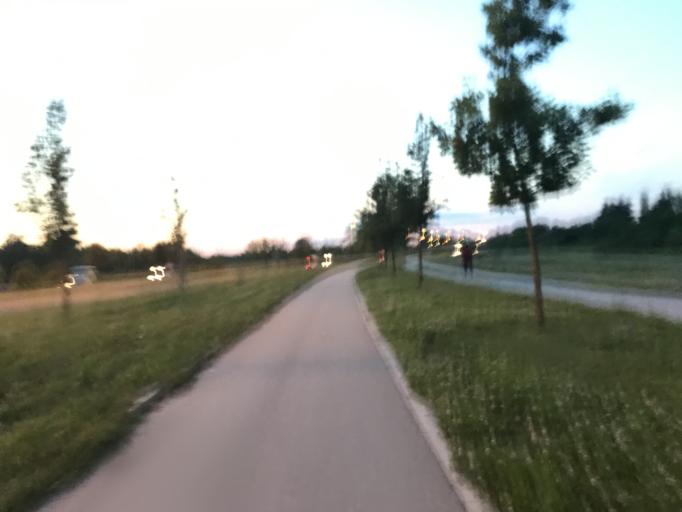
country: RS
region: Autonomna Pokrajina Vojvodina
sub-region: Juznobacki Okrug
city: Novi Sad
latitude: 45.2712
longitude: 19.8015
